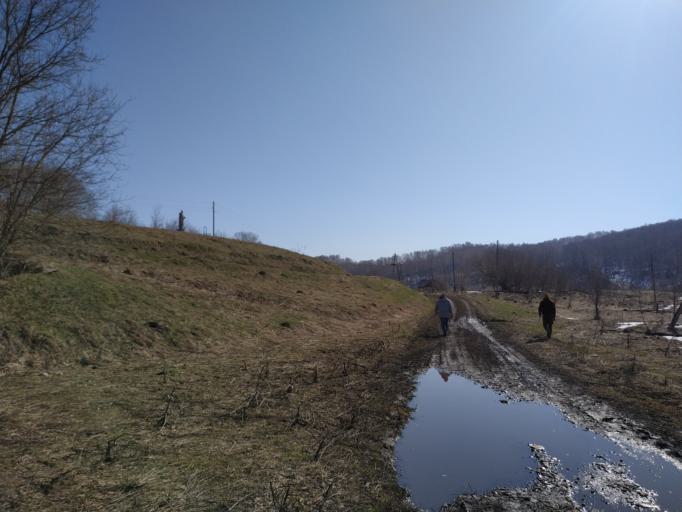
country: RU
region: Altai Krai
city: Krasnogorskoye
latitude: 52.4829
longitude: 86.2278
